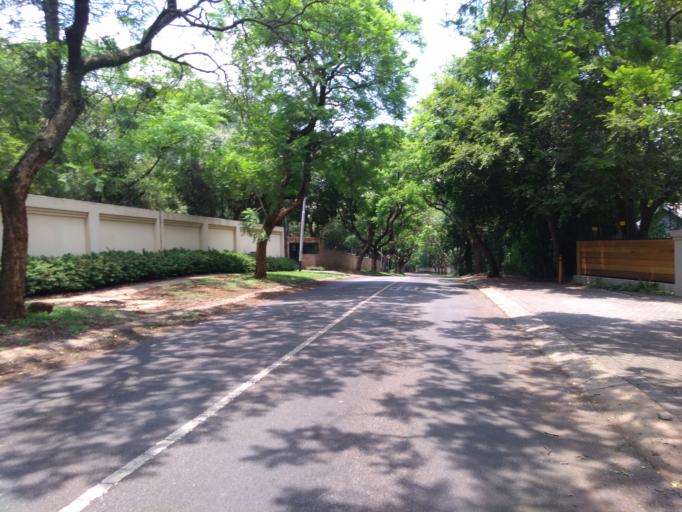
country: ZA
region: Gauteng
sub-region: City of Tshwane Metropolitan Municipality
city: Pretoria
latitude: -25.7631
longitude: 28.2290
